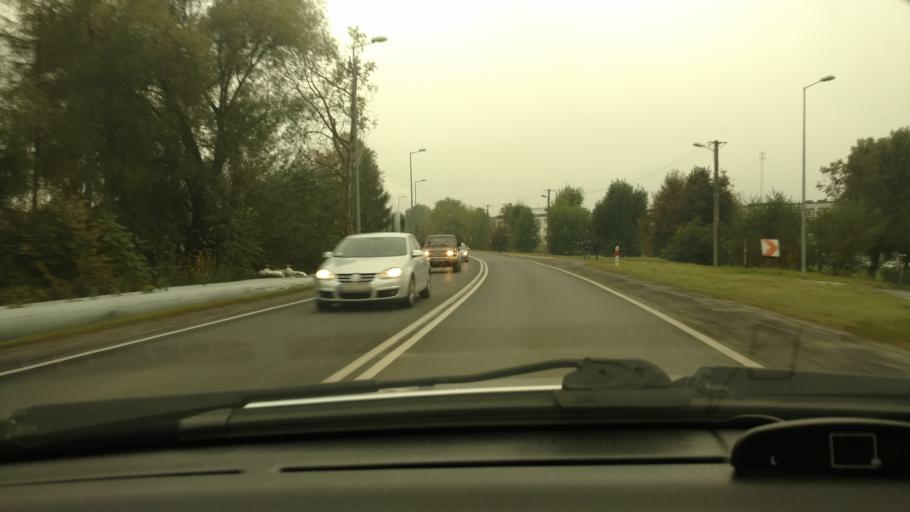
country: PL
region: Lesser Poland Voivodeship
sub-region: Powiat gorlicki
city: Gorlice
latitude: 49.6696
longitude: 21.1762
